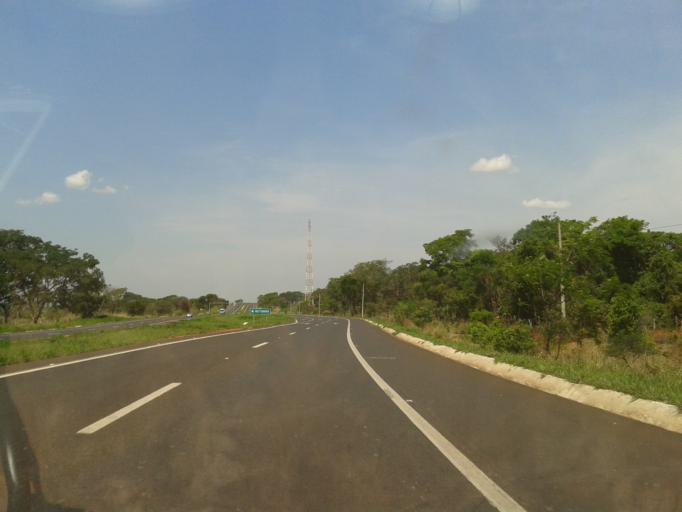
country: BR
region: Minas Gerais
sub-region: Monte Alegre De Minas
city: Monte Alegre de Minas
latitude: -18.8517
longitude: -48.7921
